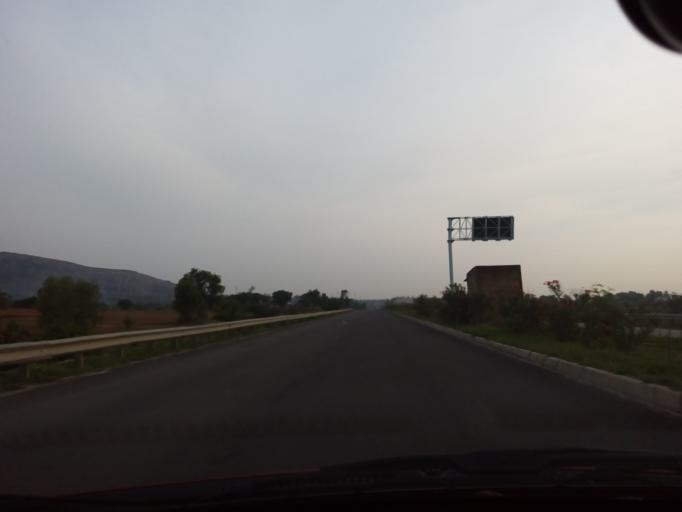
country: IN
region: Karnataka
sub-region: Chikkaballapur
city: Gudibanda
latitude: 13.6130
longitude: 77.7891
